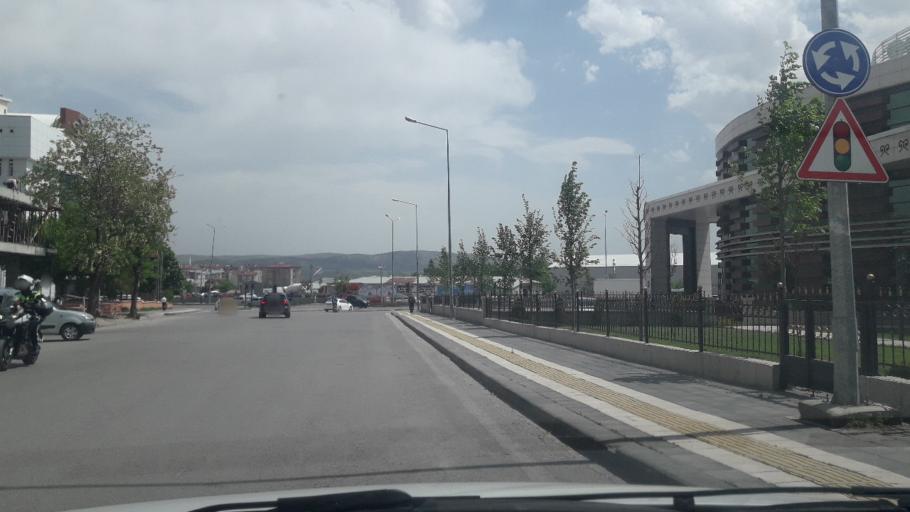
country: TR
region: Sivas
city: Sivas
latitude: 39.7425
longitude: 37.0120
